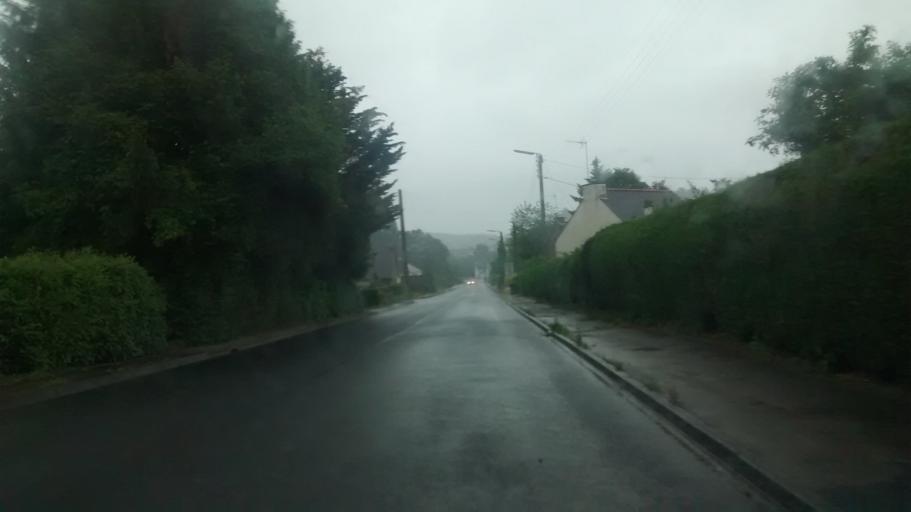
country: FR
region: Brittany
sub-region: Departement du Morbihan
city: La Gacilly
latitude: 47.7693
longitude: -2.1426
